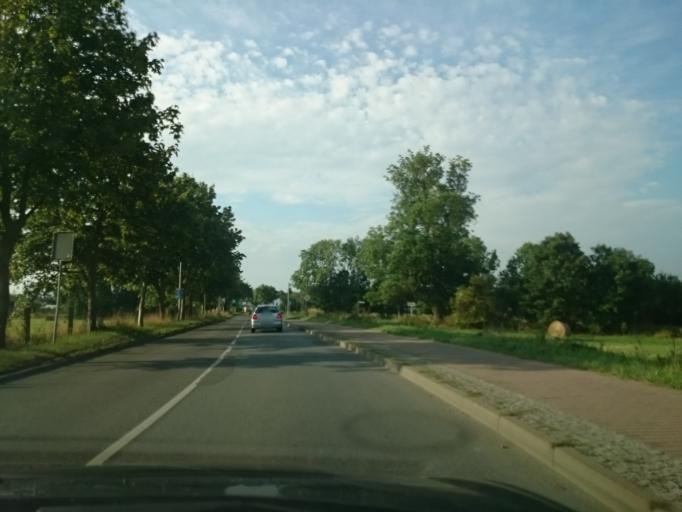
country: DE
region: Mecklenburg-Vorpommern
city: Demmin
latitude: 53.8971
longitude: 13.0409
